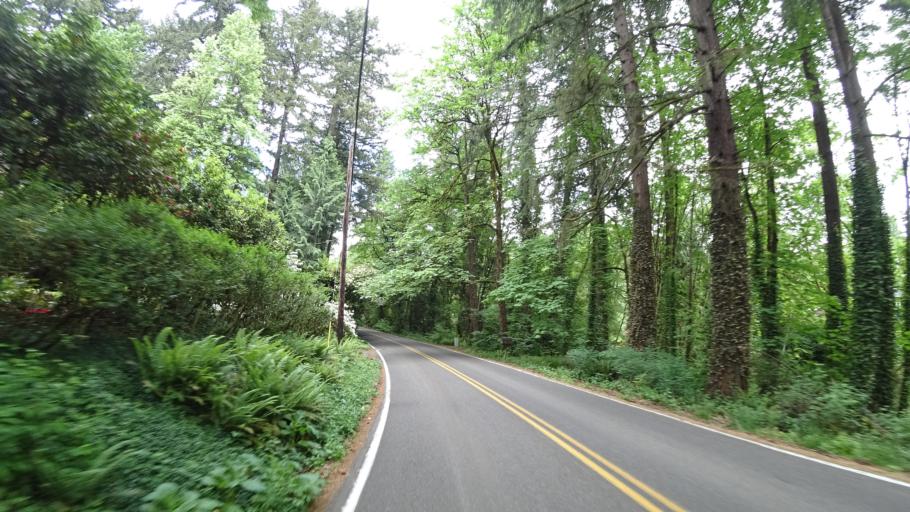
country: US
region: Oregon
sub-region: Clackamas County
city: Lake Oswego
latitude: 45.4440
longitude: -122.6640
